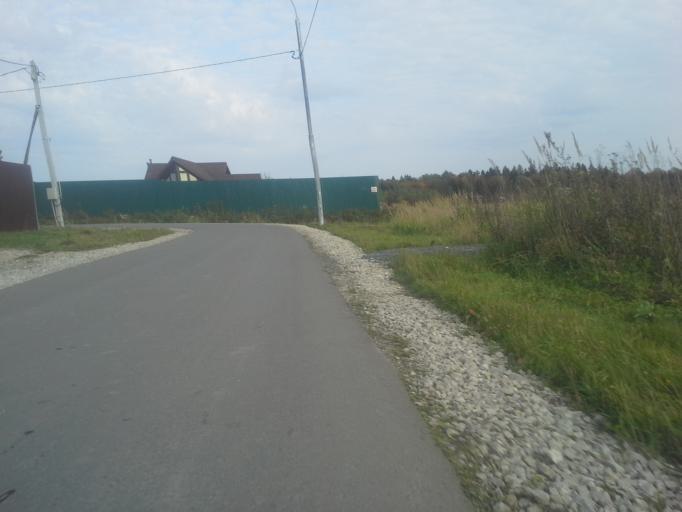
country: RU
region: Moskovskaya
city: Kievskij
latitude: 55.3968
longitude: 36.9119
